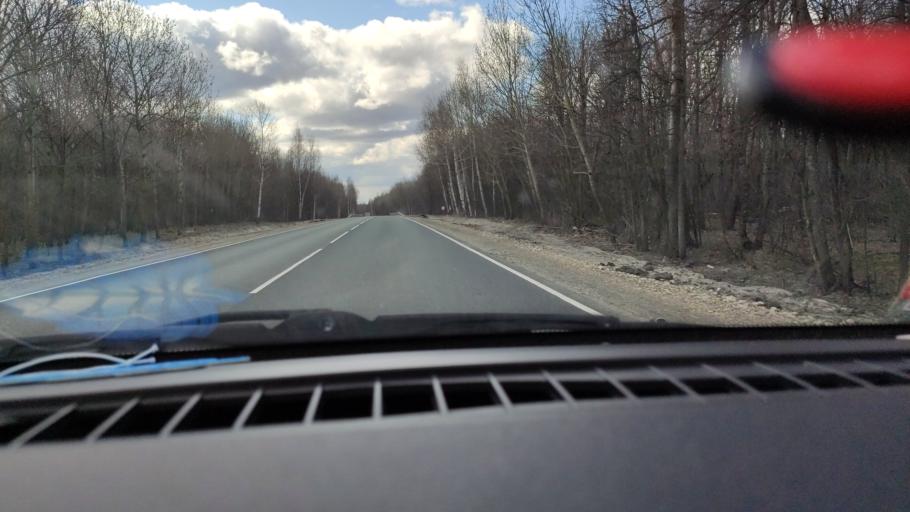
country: RU
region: Saratov
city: Khvalynsk
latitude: 52.4457
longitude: 48.0100
